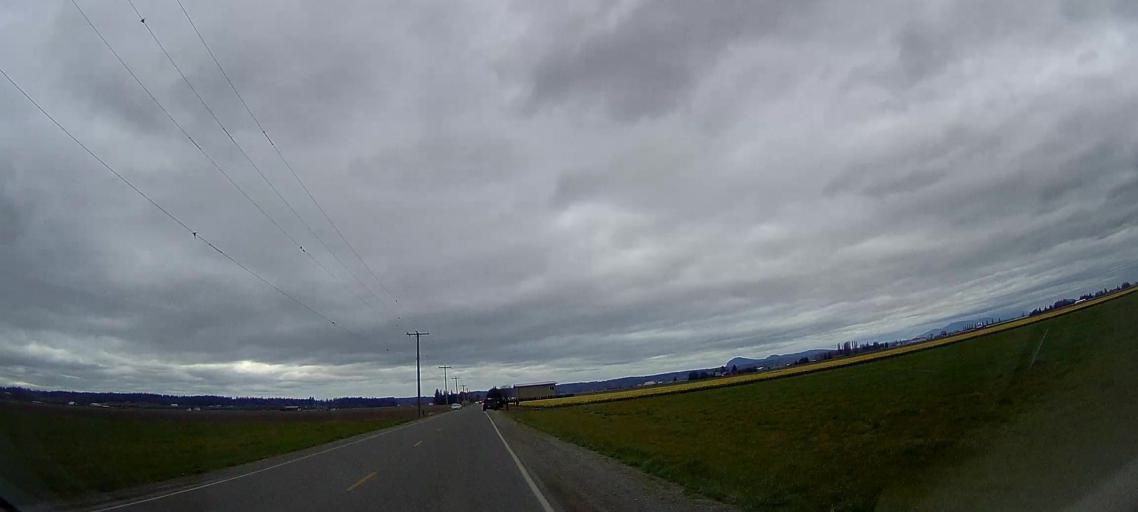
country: US
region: Washington
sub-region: Skagit County
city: Mount Vernon
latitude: 48.3996
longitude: -122.4054
